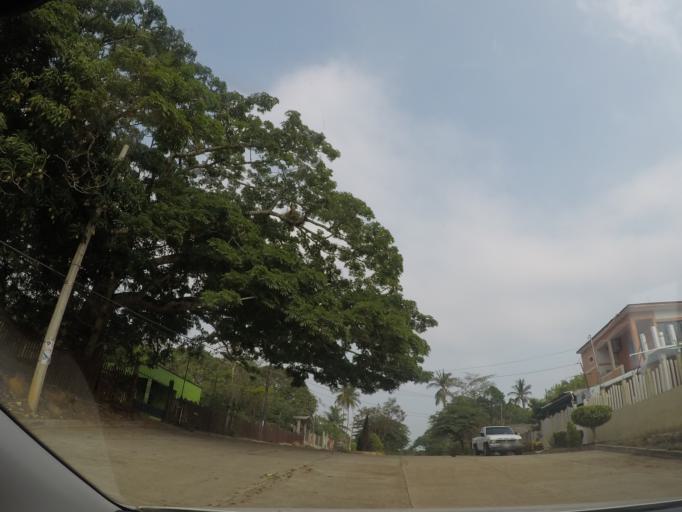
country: MX
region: Oaxaca
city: Matias Romero
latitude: 16.8810
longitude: -95.0446
